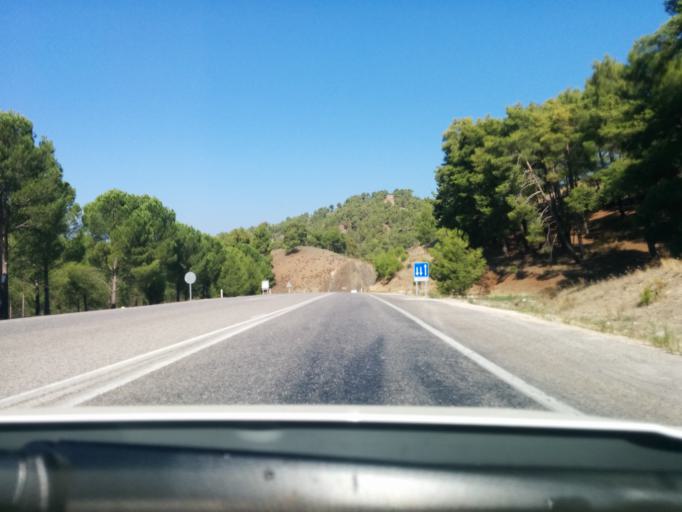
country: TR
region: Mugla
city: Kemer
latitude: 36.6189
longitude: 29.3529
